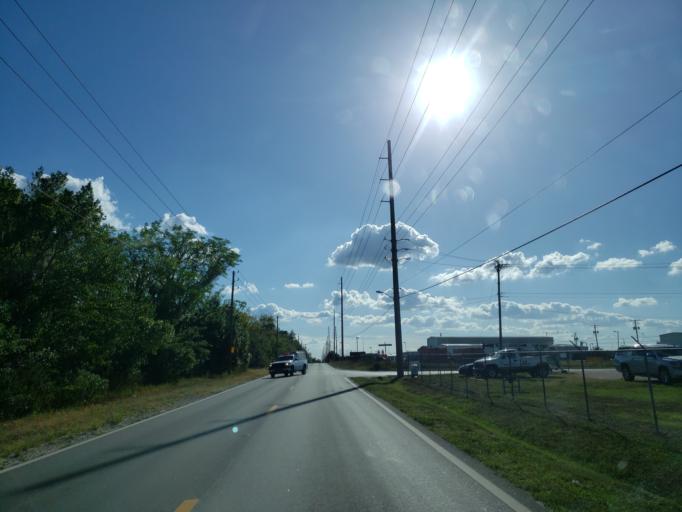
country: US
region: Florida
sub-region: Hillsborough County
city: Plant City
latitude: 27.9937
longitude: -82.1590
